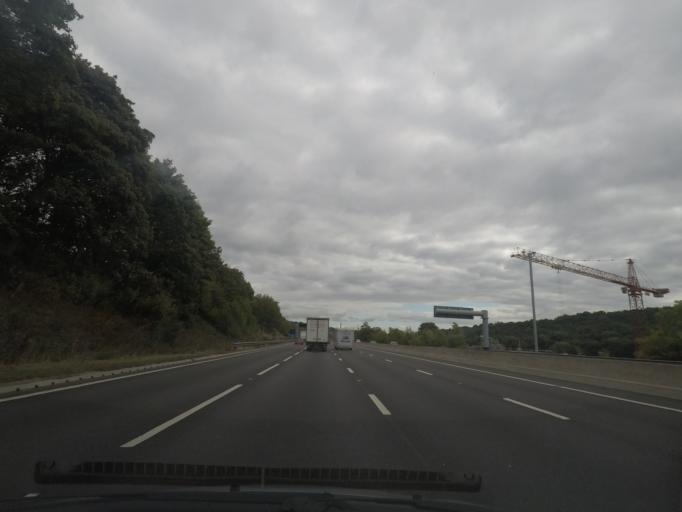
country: GB
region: England
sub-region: Rotherham
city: Wentworth
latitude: 53.4369
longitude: -1.4317
